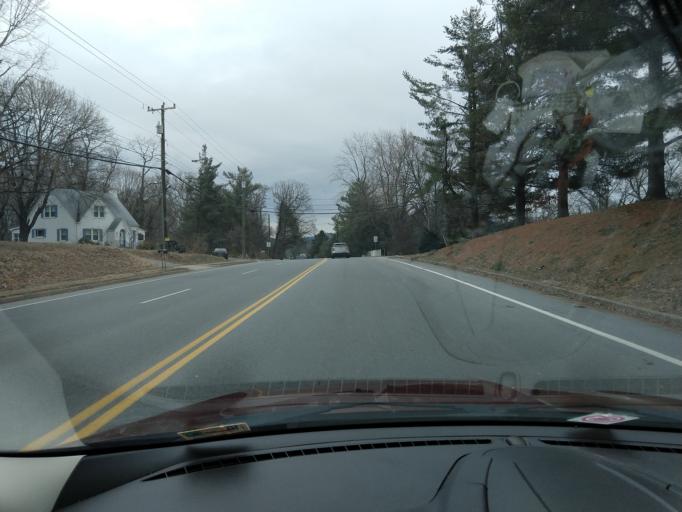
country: US
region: Virginia
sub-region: City of Waynesboro
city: Waynesboro
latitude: 38.0686
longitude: -78.9177
